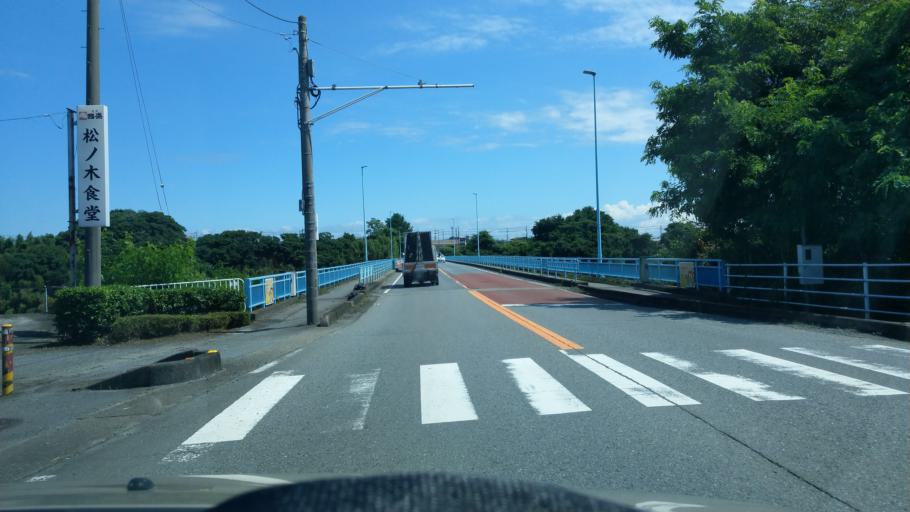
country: JP
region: Saitama
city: Yorii
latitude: 36.1192
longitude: 139.2115
